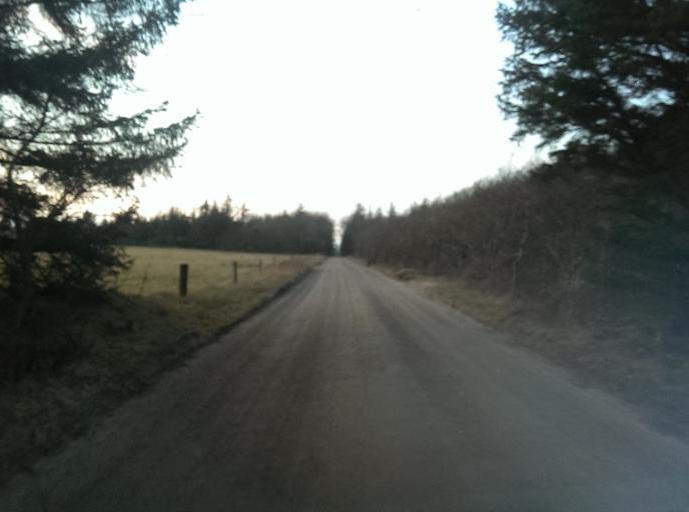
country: DK
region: South Denmark
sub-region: Varde Kommune
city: Oksbol
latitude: 55.5626
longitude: 8.3135
